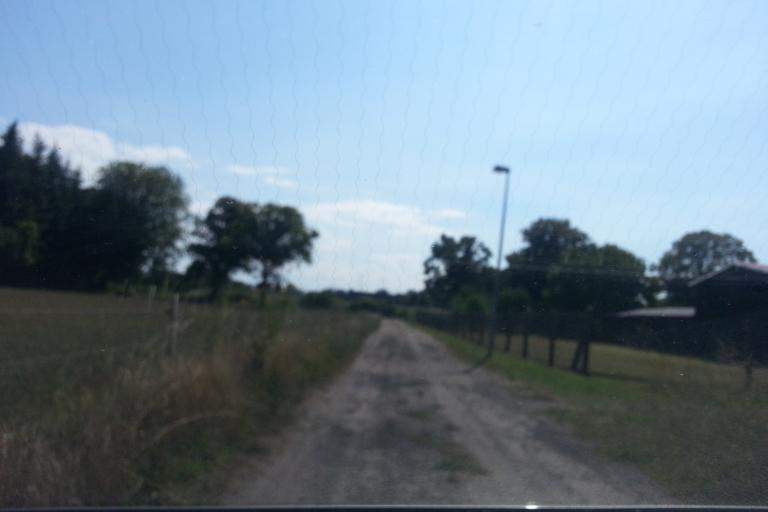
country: DE
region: Mecklenburg-Vorpommern
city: Ducherow
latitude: 53.7157
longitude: 13.7867
